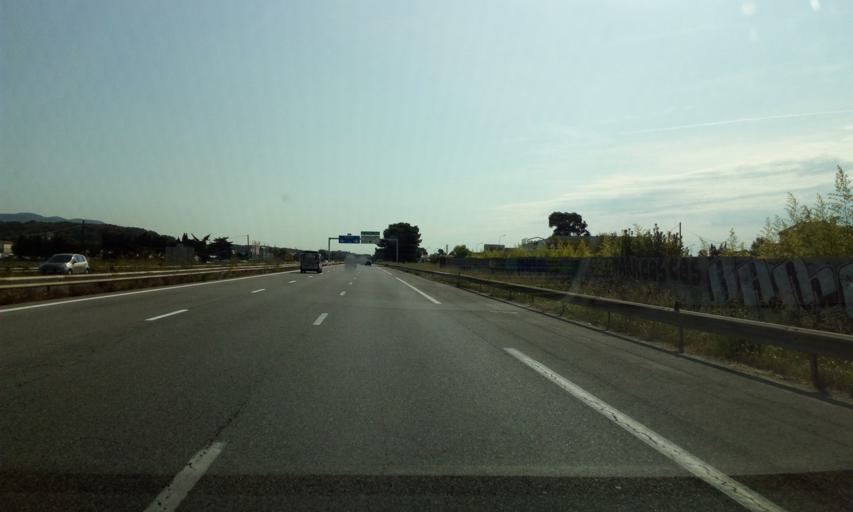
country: FR
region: Provence-Alpes-Cote d'Azur
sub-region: Departement du Var
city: Ollioules
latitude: 43.1207
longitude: 5.8392
